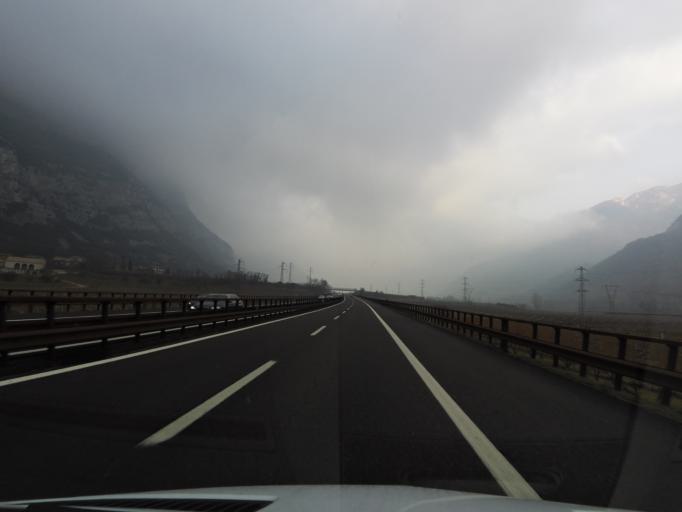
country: IT
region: Veneto
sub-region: Provincia di Verona
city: Dolce
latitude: 45.6201
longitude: 10.8606
